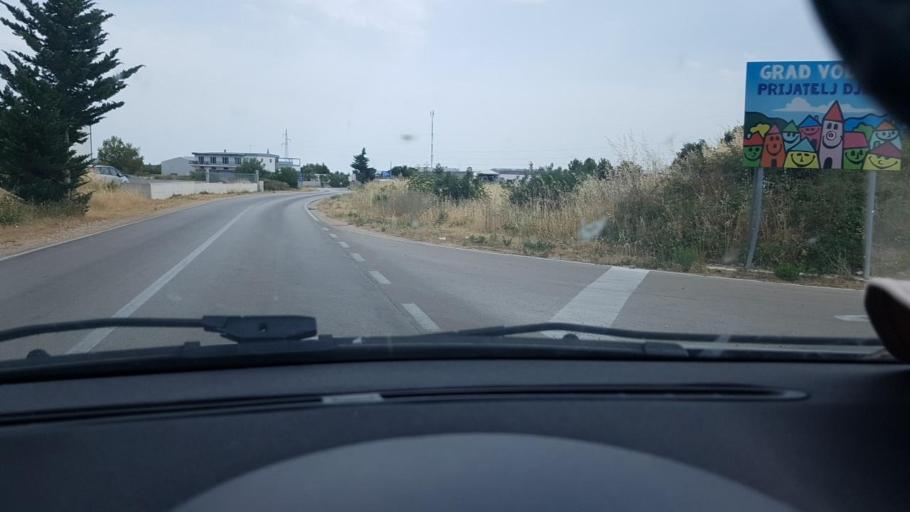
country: HR
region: Sibensko-Kniniska
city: Vodice
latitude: 43.7724
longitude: 15.7724
